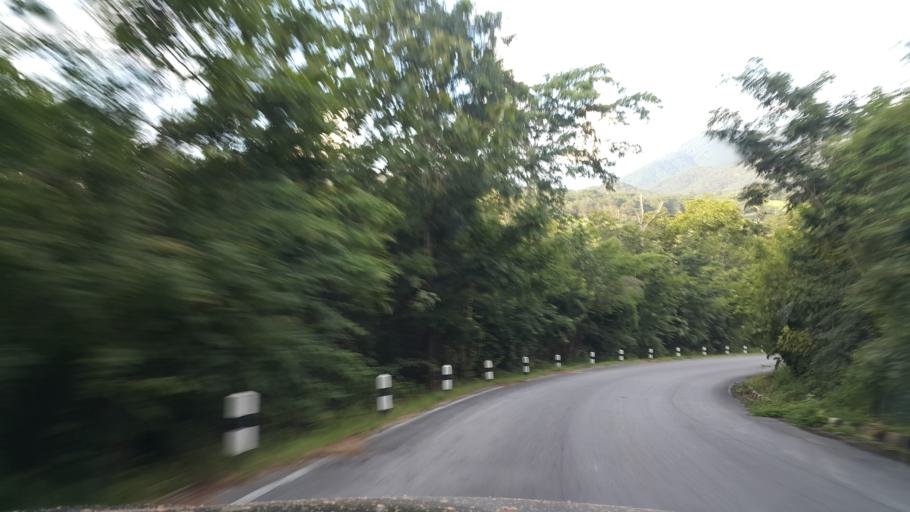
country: TH
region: Mae Hong Son
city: Mae Hi
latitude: 19.1916
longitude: 98.4184
